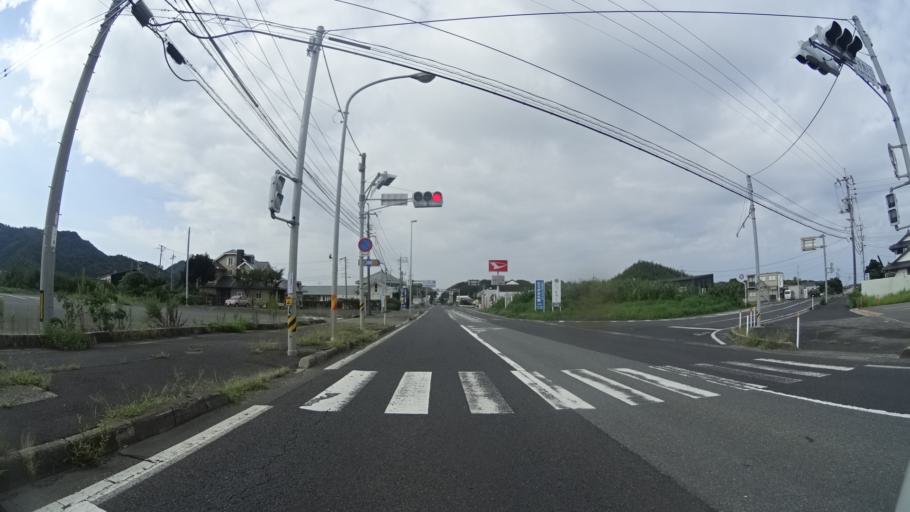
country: JP
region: Shimane
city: Odacho-oda
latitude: 35.2231
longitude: 132.5149
